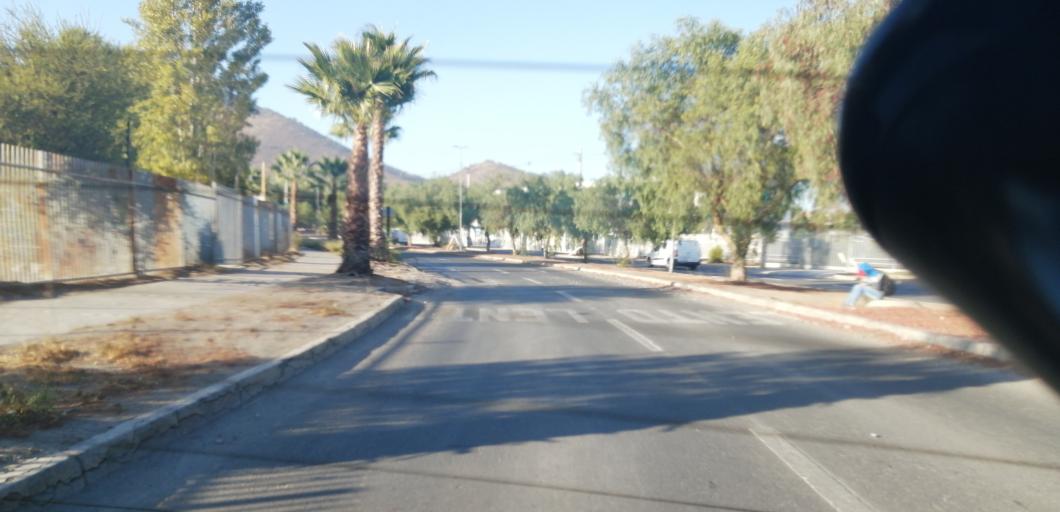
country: CL
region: Santiago Metropolitan
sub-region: Provincia de Santiago
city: Lo Prado
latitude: -33.4505
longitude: -70.8502
